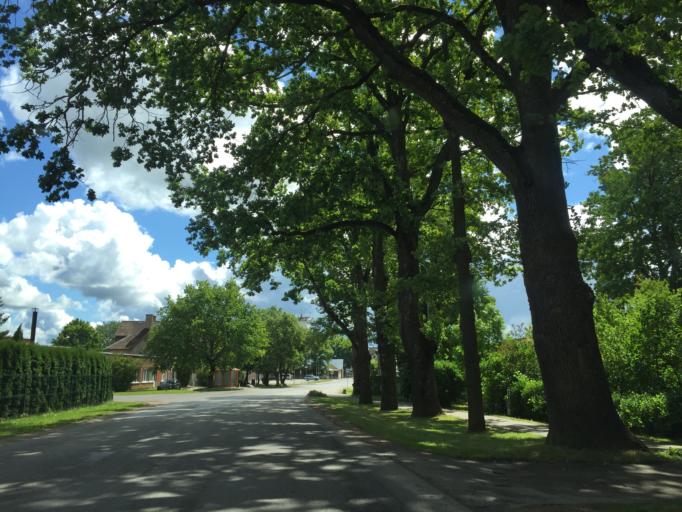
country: LV
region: Lecava
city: Iecava
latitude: 56.5957
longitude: 24.2037
